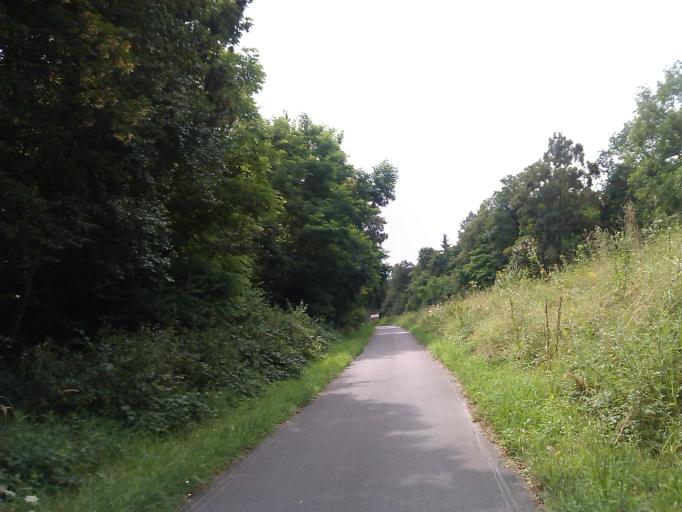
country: DE
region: Rheinland-Pfalz
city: Schifferstadt
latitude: 49.3579
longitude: 8.4037
